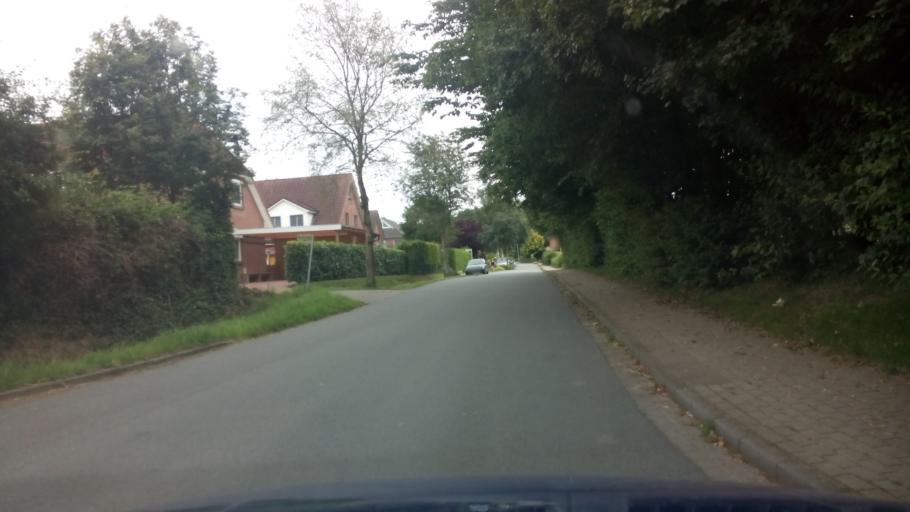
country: DE
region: Lower Saxony
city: Hambergen
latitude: 53.3065
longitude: 8.8264
